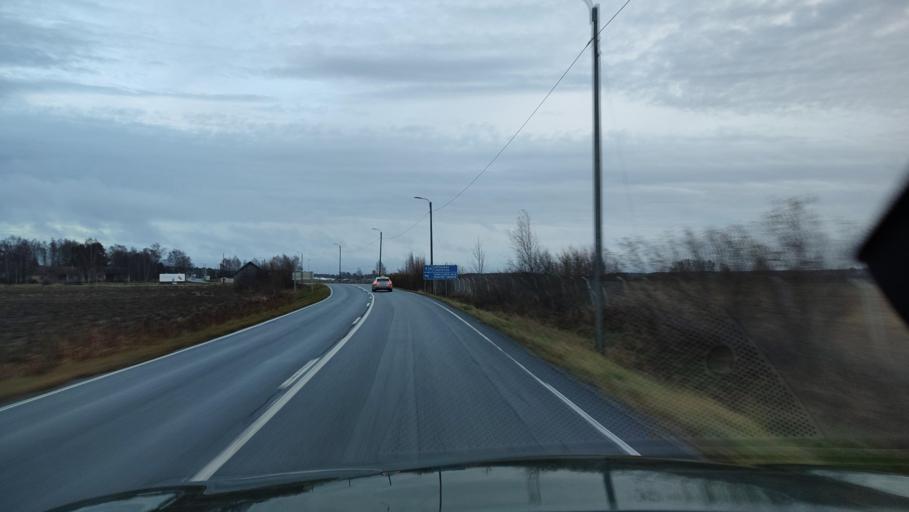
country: FI
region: Ostrobothnia
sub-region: Vaasa
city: Ristinummi
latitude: 63.0445
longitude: 21.7499
